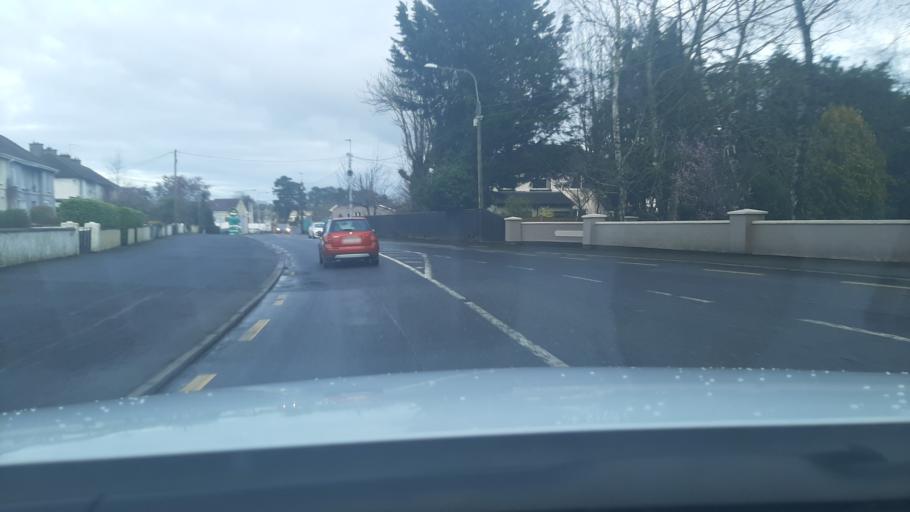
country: IE
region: Leinster
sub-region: Kildare
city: Kildare
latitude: 53.1536
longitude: -6.8967
